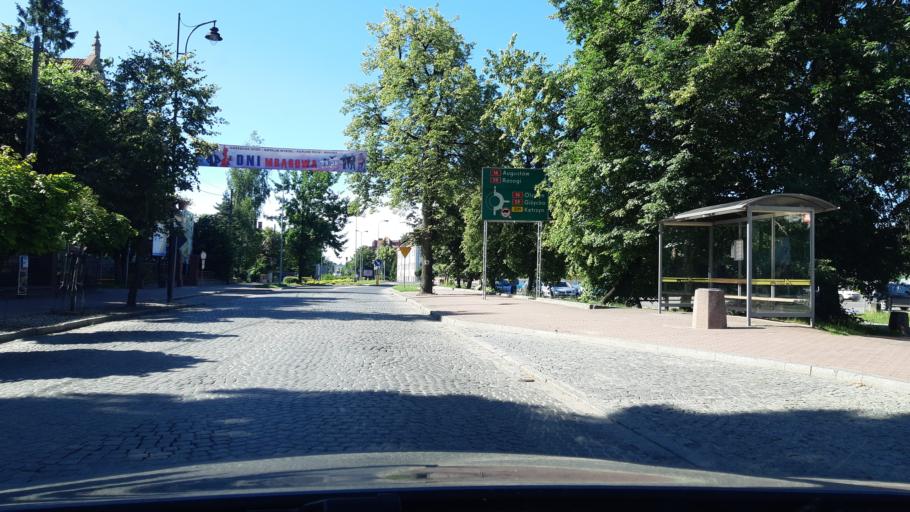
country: PL
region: Warmian-Masurian Voivodeship
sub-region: Powiat mragowski
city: Mragowo
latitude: 53.8654
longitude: 21.3054
